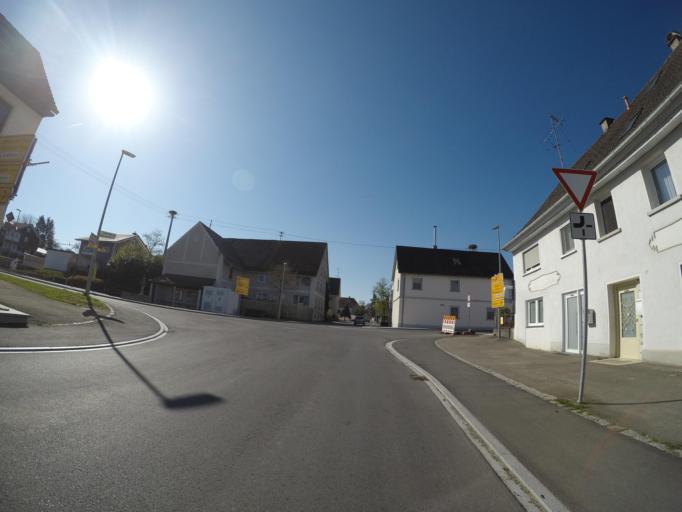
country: DE
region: Baden-Wuerttemberg
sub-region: Tuebingen Region
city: Ebenweiler
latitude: 47.9006
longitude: 9.5131
